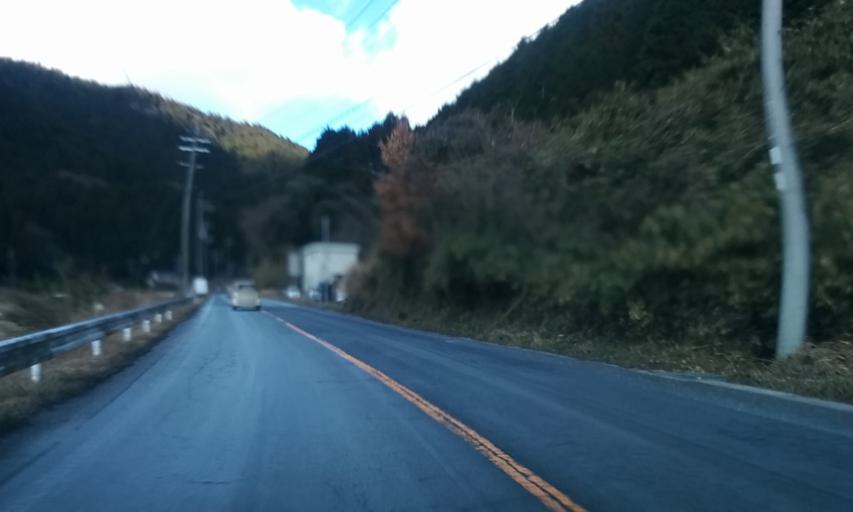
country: JP
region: Kyoto
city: Fukuchiyama
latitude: 35.3861
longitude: 135.0431
